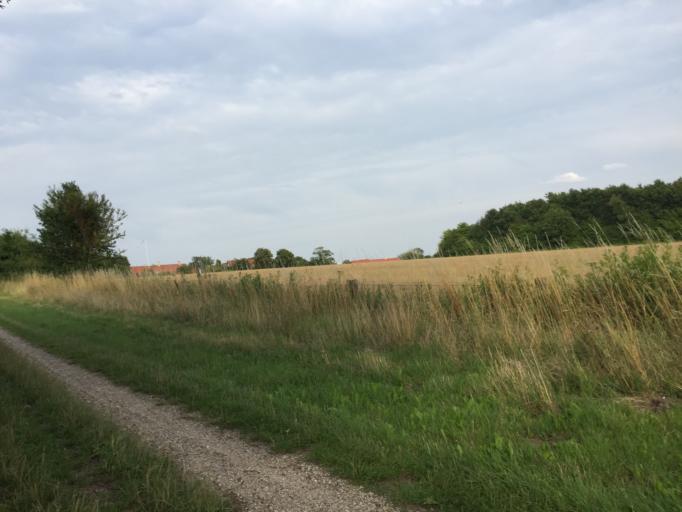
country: DK
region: South Denmark
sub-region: Odense Kommune
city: Neder Holluf
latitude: 55.3846
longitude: 10.4660
